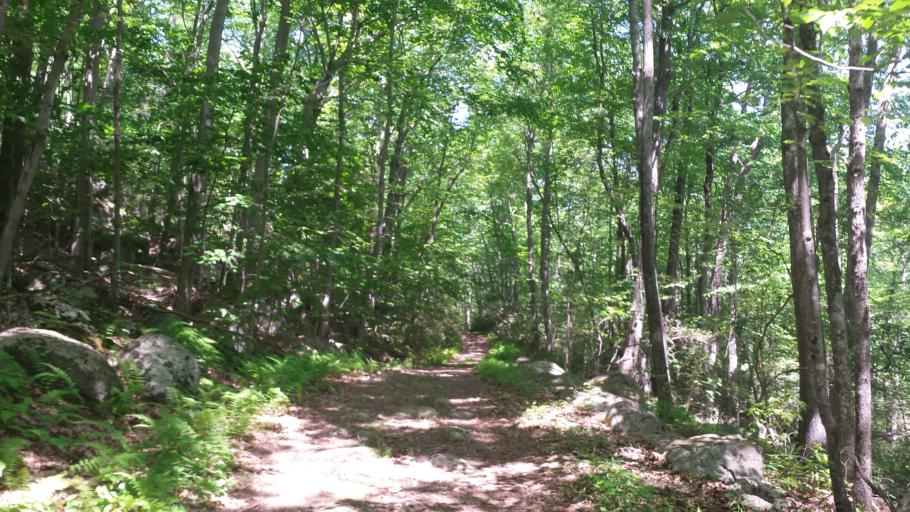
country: US
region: New York
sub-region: Westchester County
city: Pound Ridge
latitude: 41.2557
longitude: -73.5721
